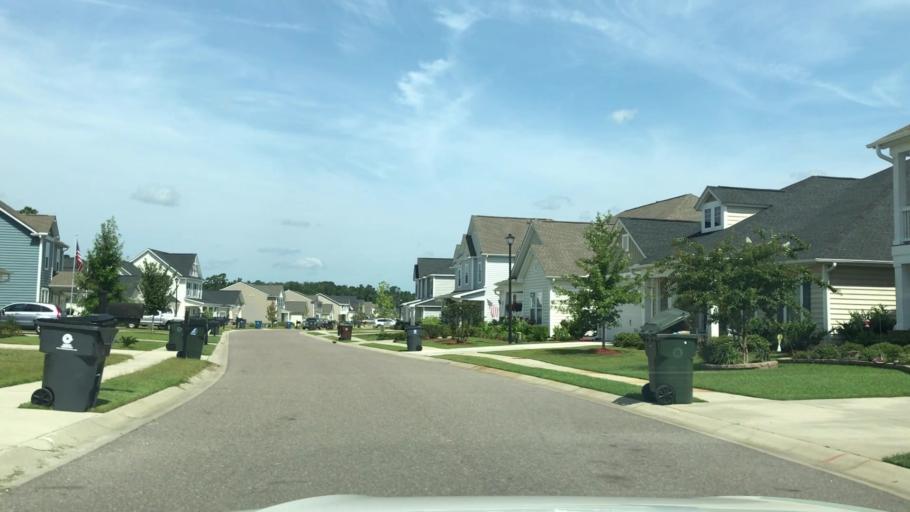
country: US
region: South Carolina
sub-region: Berkeley County
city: Moncks Corner
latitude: 33.1057
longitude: -80.0428
